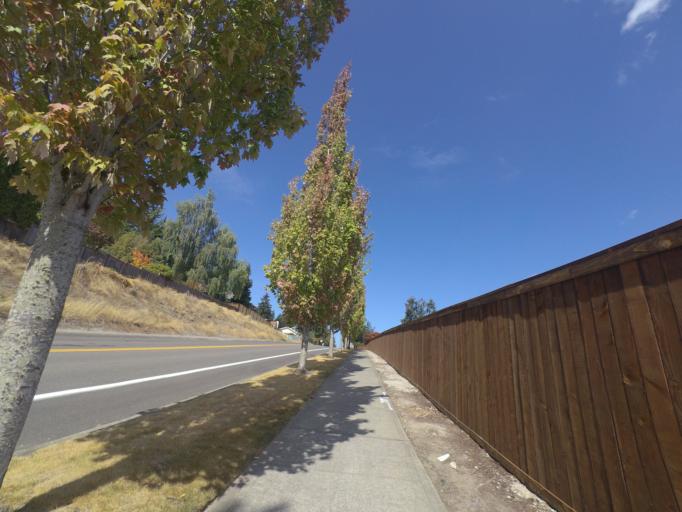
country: US
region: Washington
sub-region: Pierce County
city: Fircrest
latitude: 47.2089
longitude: -122.5159
